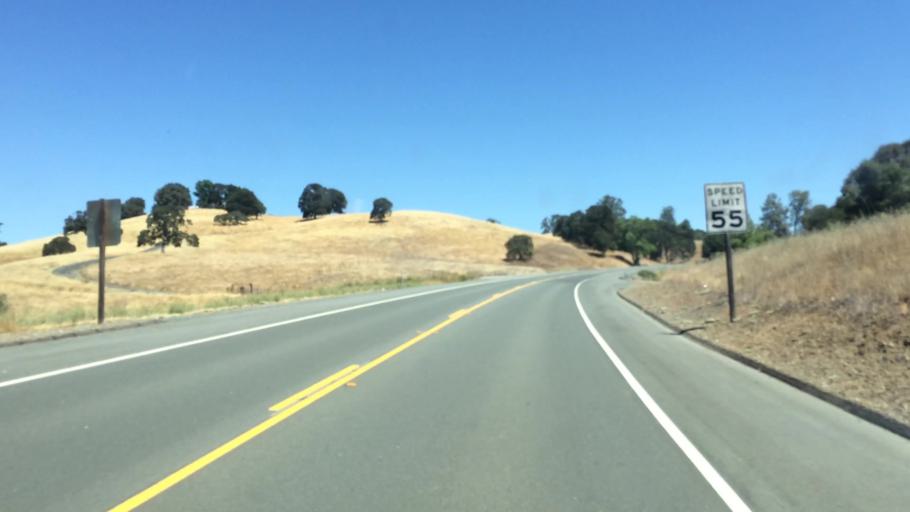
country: US
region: California
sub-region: Amador County
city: Plymouth
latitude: 38.4363
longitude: -120.8774
